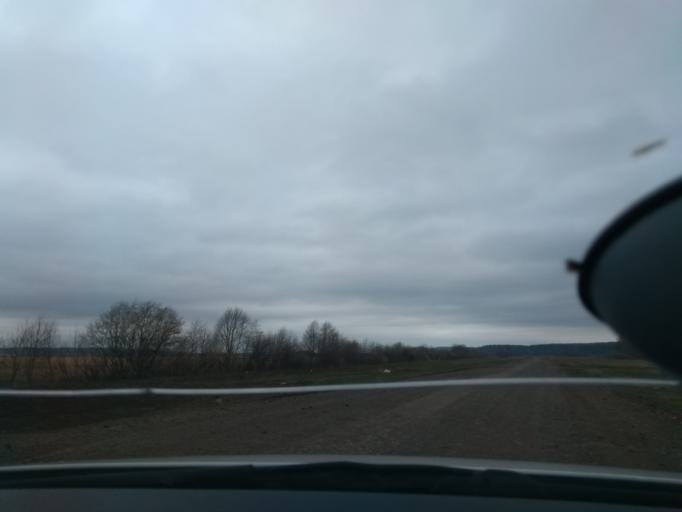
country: RU
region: Perm
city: Orda
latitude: 57.2255
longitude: 56.5991
